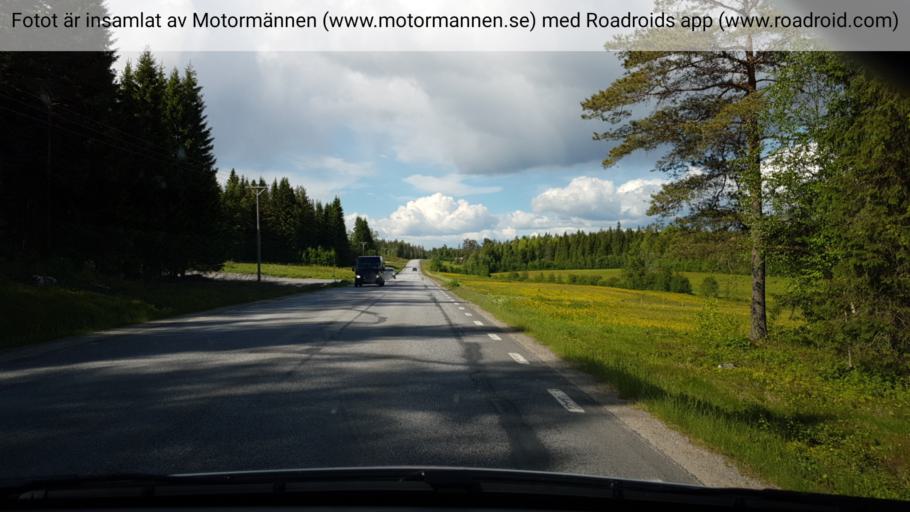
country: SE
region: Vaesterbotten
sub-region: Umea Kommun
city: Roback
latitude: 63.8888
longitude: 20.1985
